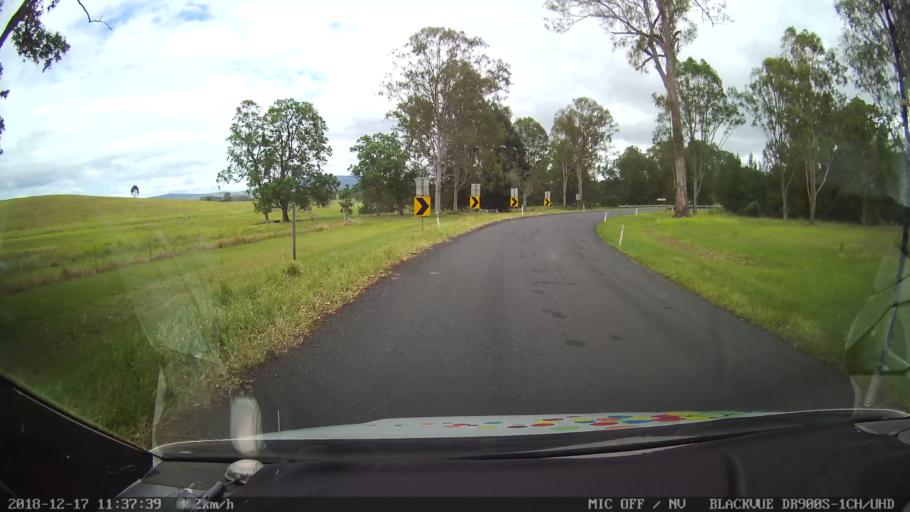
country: AU
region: New South Wales
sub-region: Kyogle
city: Kyogle
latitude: -28.7029
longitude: 152.6028
